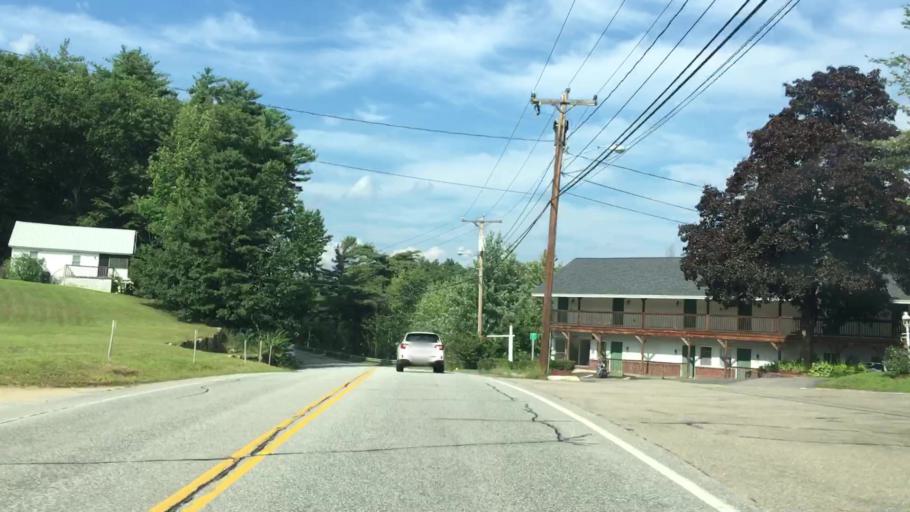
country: US
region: New Hampshire
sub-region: Belknap County
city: Laconia
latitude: 43.4952
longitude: -71.5200
